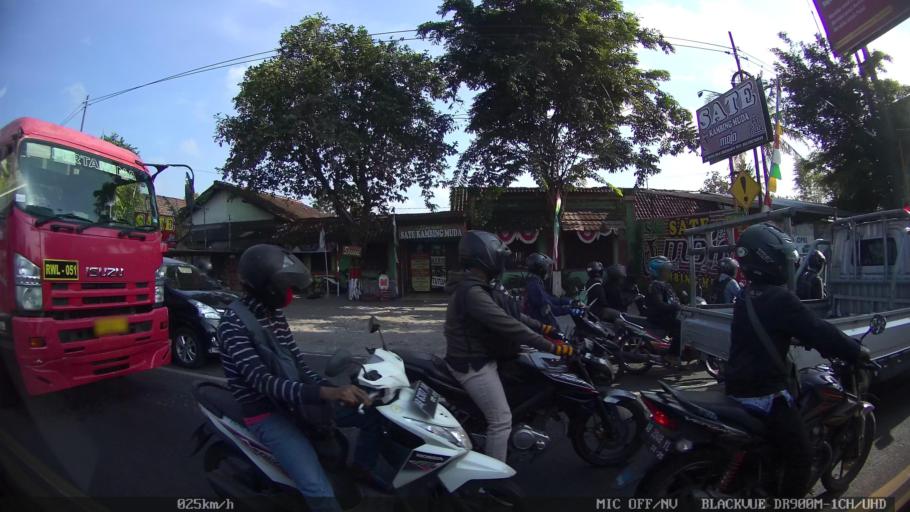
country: ID
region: Daerah Istimewa Yogyakarta
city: Gamping Lor
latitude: -7.8030
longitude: 110.3100
